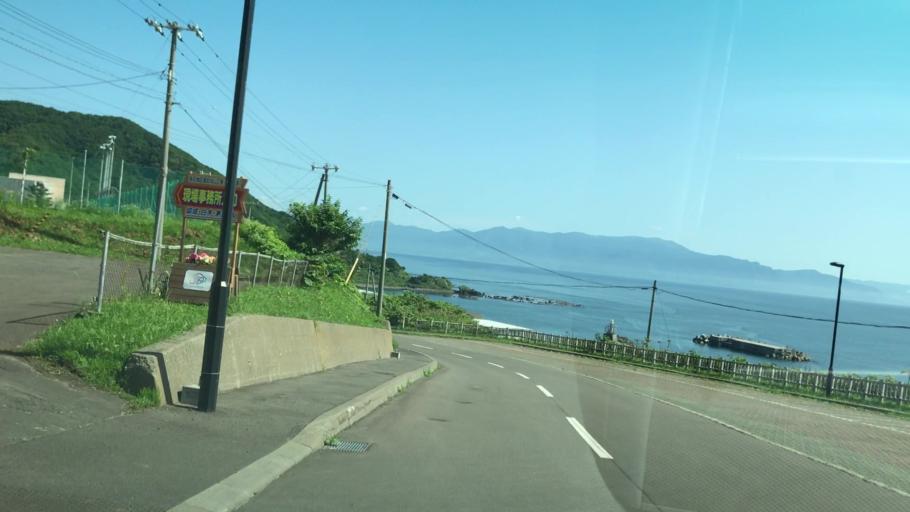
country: JP
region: Hokkaido
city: Iwanai
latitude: 43.1460
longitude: 140.4233
